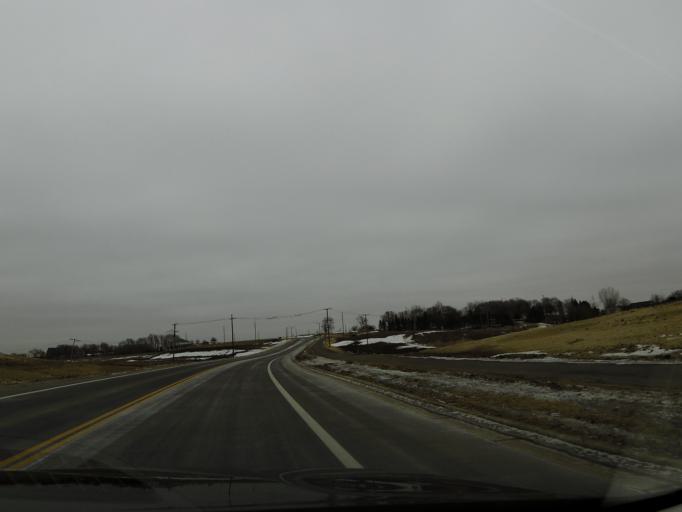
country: US
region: Minnesota
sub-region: Carver County
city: Waconia
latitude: 44.8395
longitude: -93.8231
